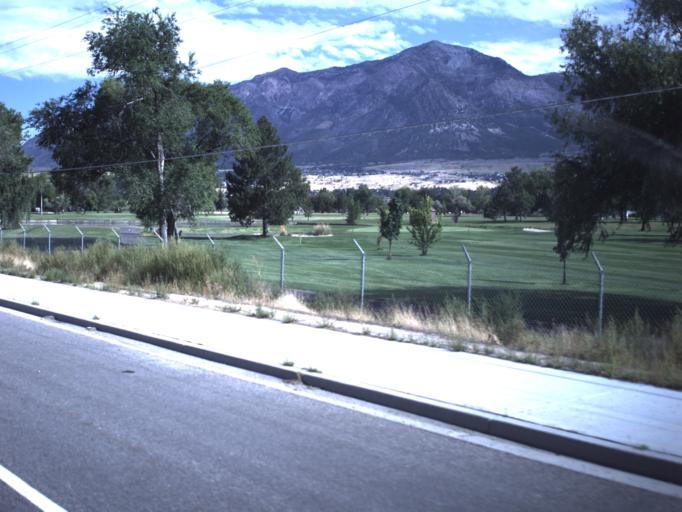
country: US
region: Utah
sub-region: Weber County
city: Harrisville
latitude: 41.2886
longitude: -111.9905
